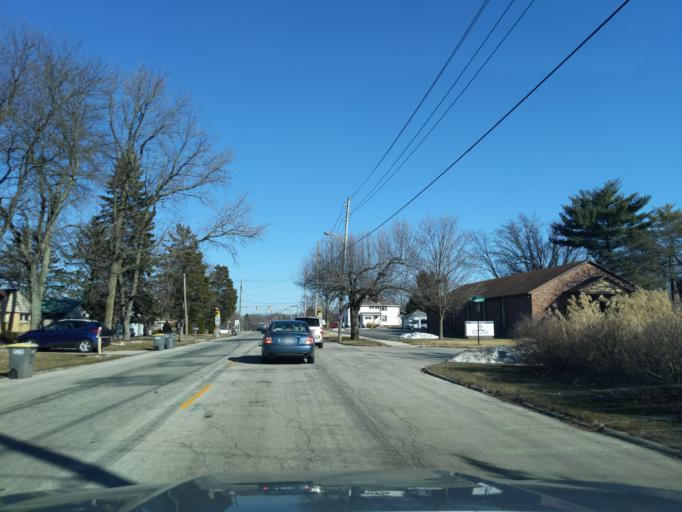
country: US
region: Indiana
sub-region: Tippecanoe County
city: West Lafayette
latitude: 40.4457
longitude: -86.9162
